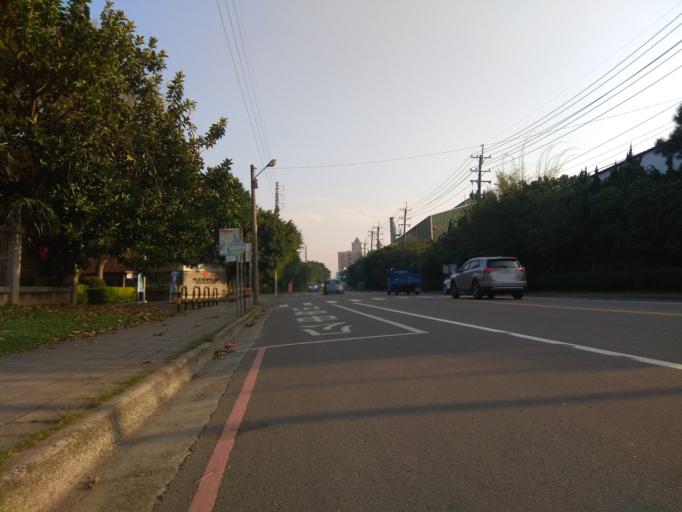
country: TW
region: Taiwan
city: Daxi
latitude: 24.9259
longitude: 121.1756
